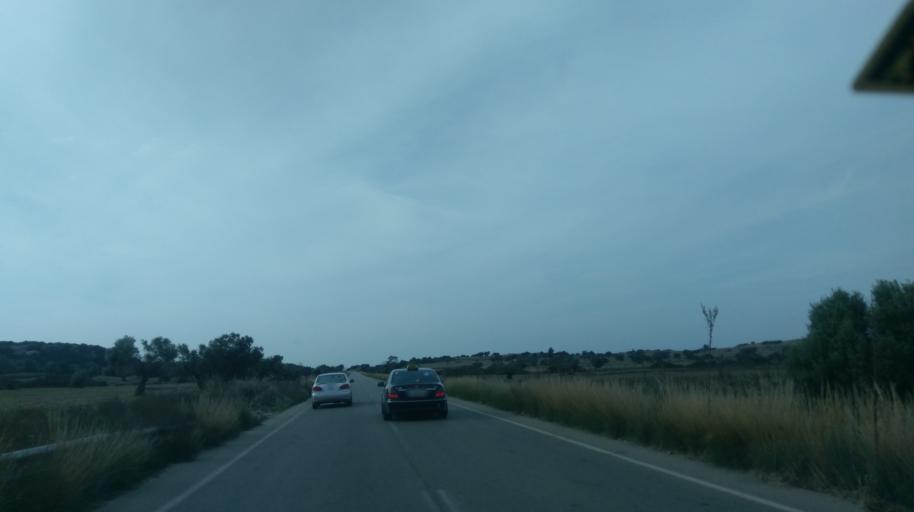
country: CY
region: Ammochostos
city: Leonarisso
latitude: 35.4012
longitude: 34.0936
